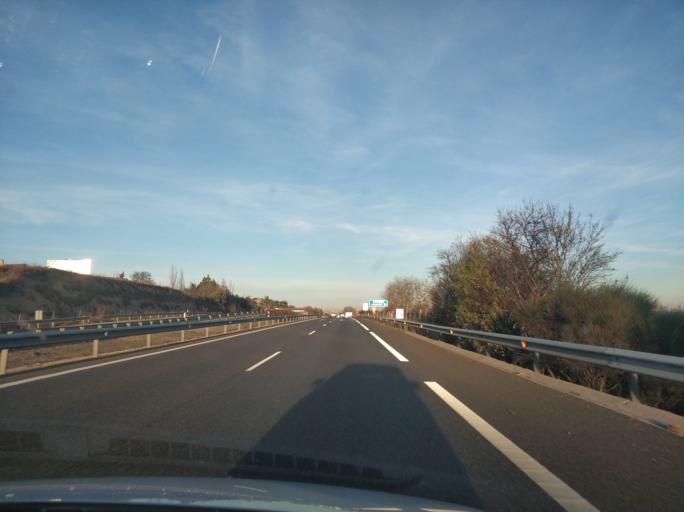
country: ES
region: Castille and Leon
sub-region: Provincia de Valladolid
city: Geria
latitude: 41.5639
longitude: -4.8634
